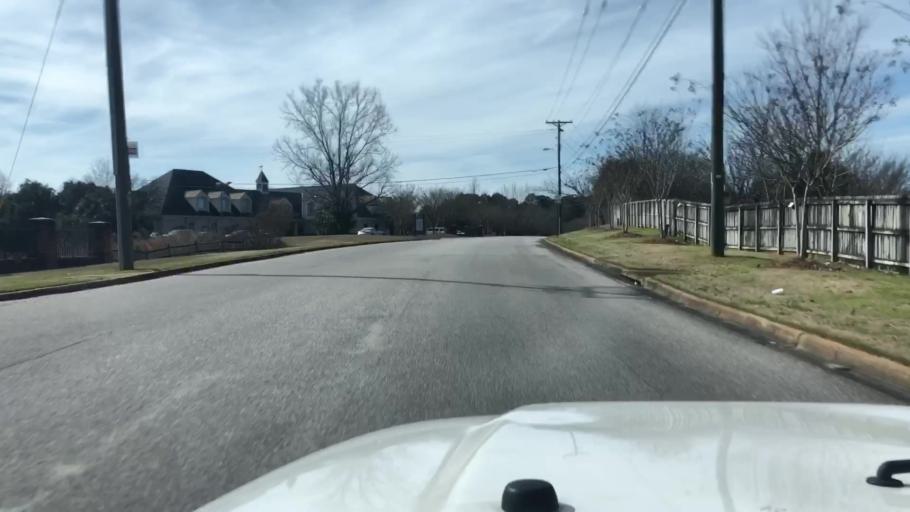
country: US
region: Alabama
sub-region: Montgomery County
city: Pike Road
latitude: 32.3603
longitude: -86.1417
